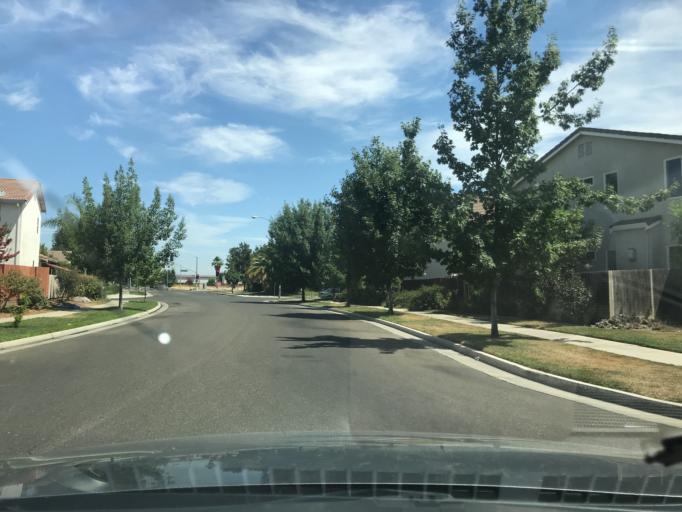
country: US
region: California
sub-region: Merced County
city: Merced
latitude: 37.3308
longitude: -120.4953
